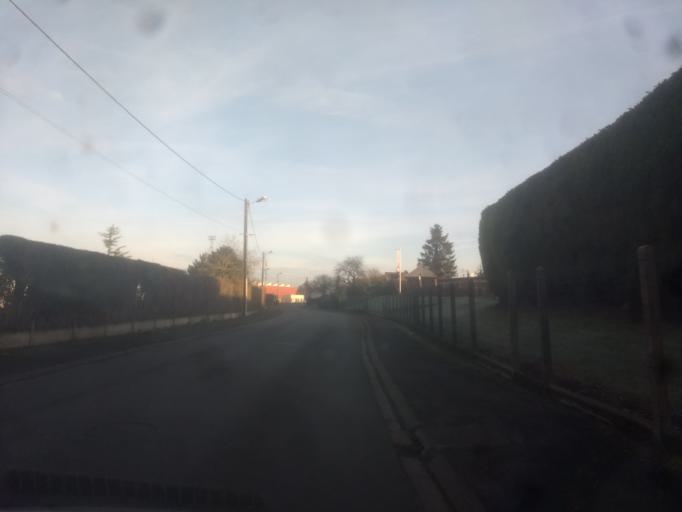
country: FR
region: Nord-Pas-de-Calais
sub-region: Departement du Pas-de-Calais
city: Achicourt
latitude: 50.2793
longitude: 2.7715
